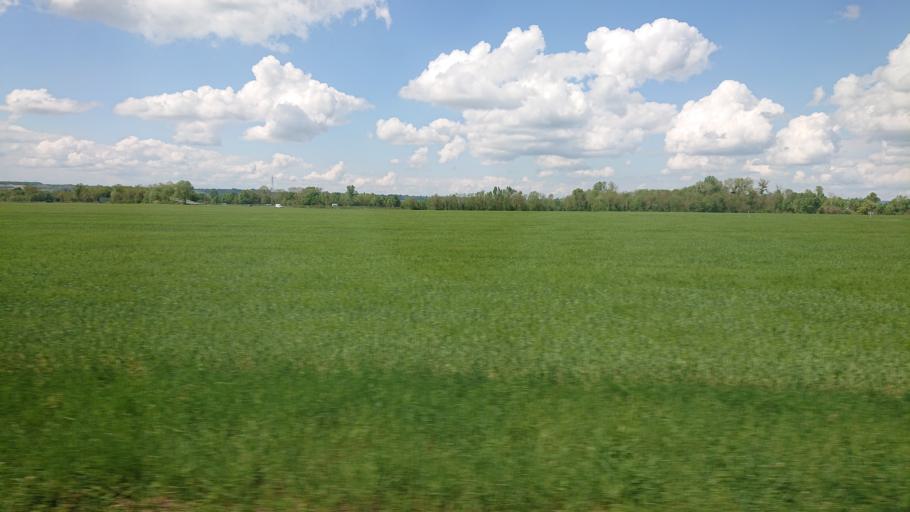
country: FR
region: Rhone-Alpes
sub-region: Departement de l'Ain
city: Leyment
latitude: 45.9435
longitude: 5.3031
